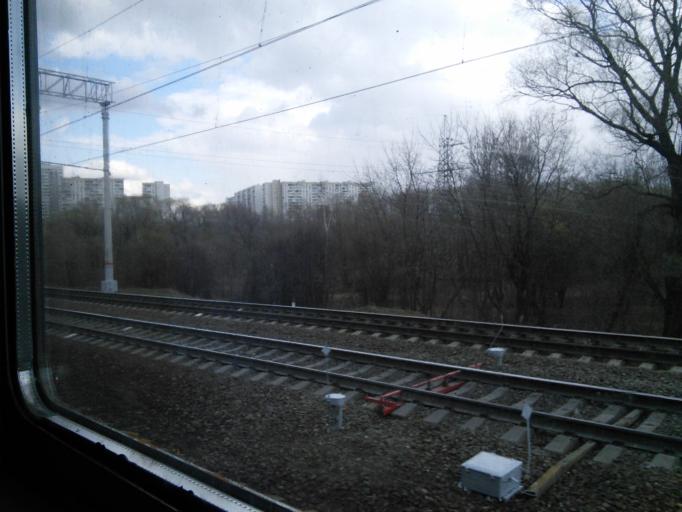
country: RU
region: Moscow
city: Orekhovo-Borisovo Severnoye
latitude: 55.6355
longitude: 37.6865
